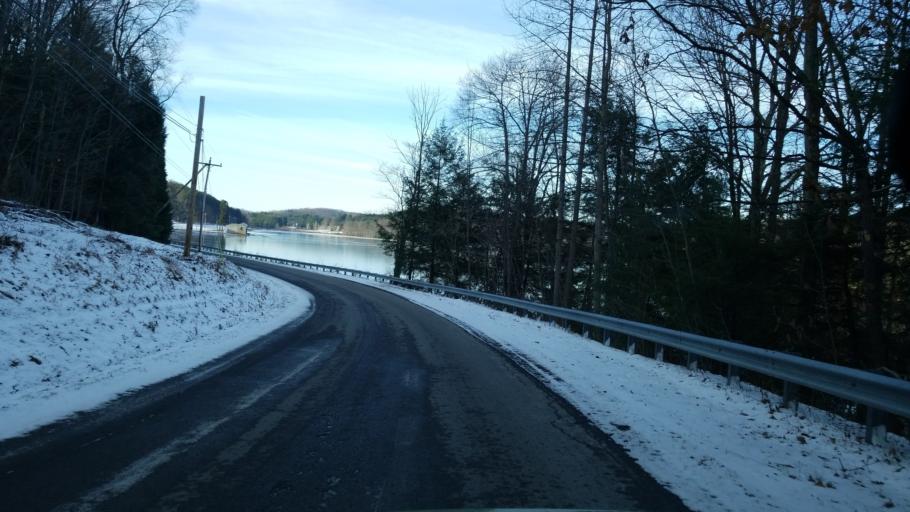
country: US
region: Pennsylvania
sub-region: Clearfield County
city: Treasure Lake
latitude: 41.0981
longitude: -78.6367
